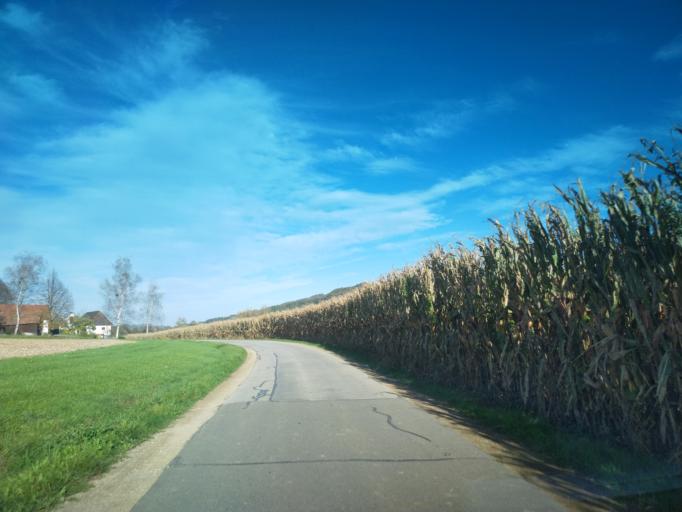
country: AT
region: Styria
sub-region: Politischer Bezirk Leibnitz
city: Sankt Johann im Saggautal
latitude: 46.7012
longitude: 15.3886
